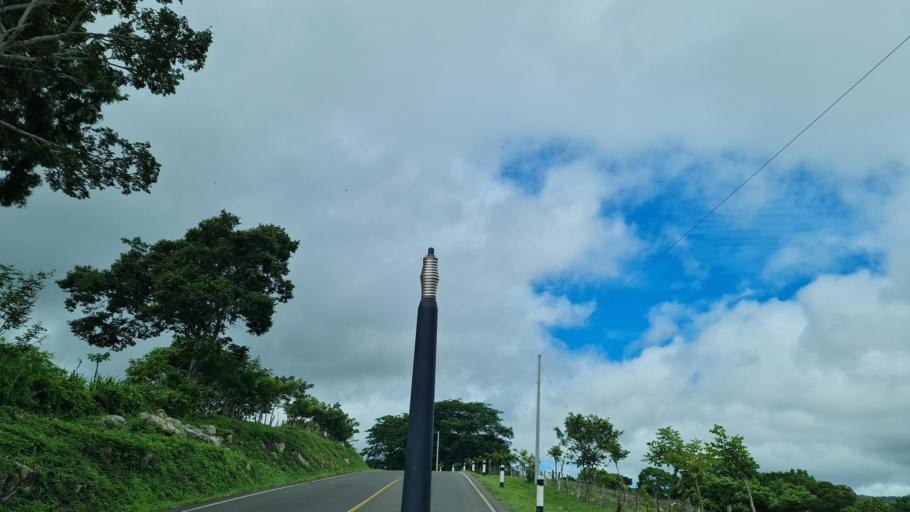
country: NI
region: Boaco
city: San Jose de los Remates
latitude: 12.6048
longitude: -85.8983
